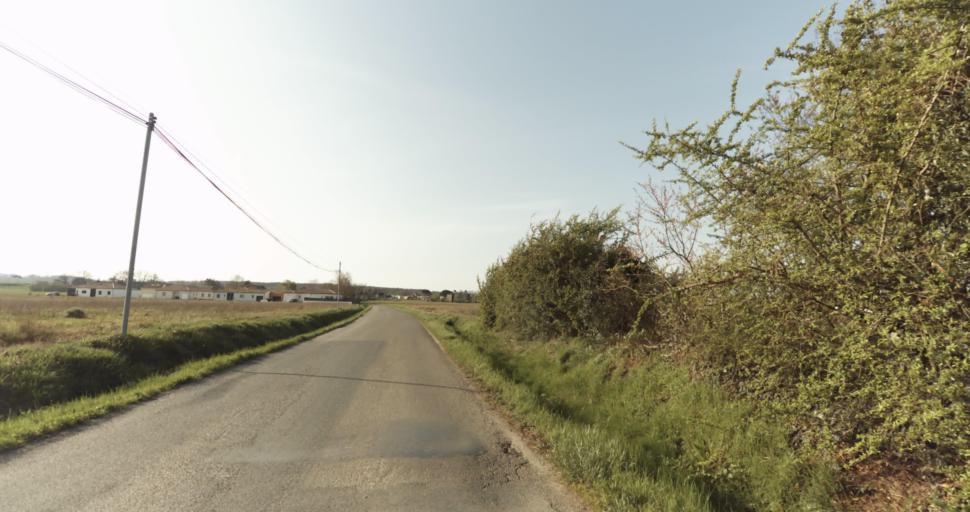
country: FR
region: Midi-Pyrenees
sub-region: Departement du Tarn
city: Saint-Sulpice-la-Pointe
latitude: 43.7643
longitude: 1.6772
